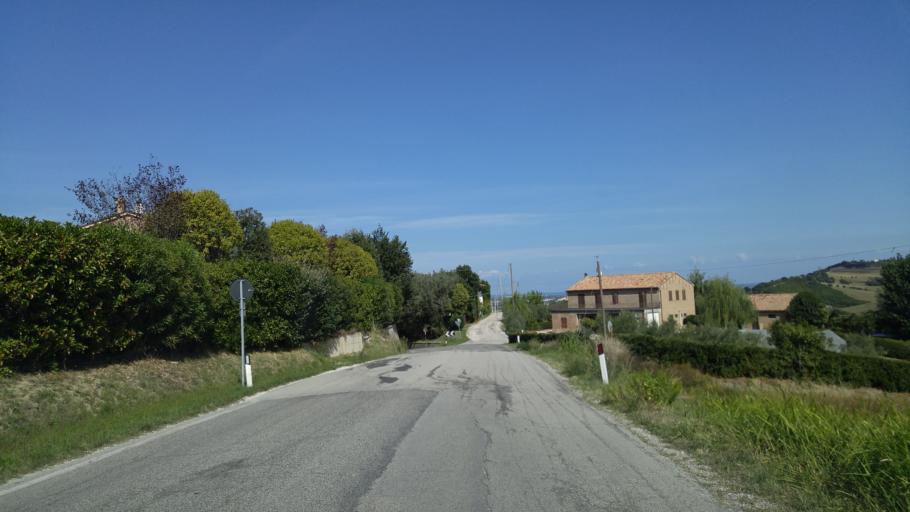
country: IT
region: The Marches
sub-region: Provincia di Pesaro e Urbino
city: Piagge
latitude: 43.7522
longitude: 12.9716
